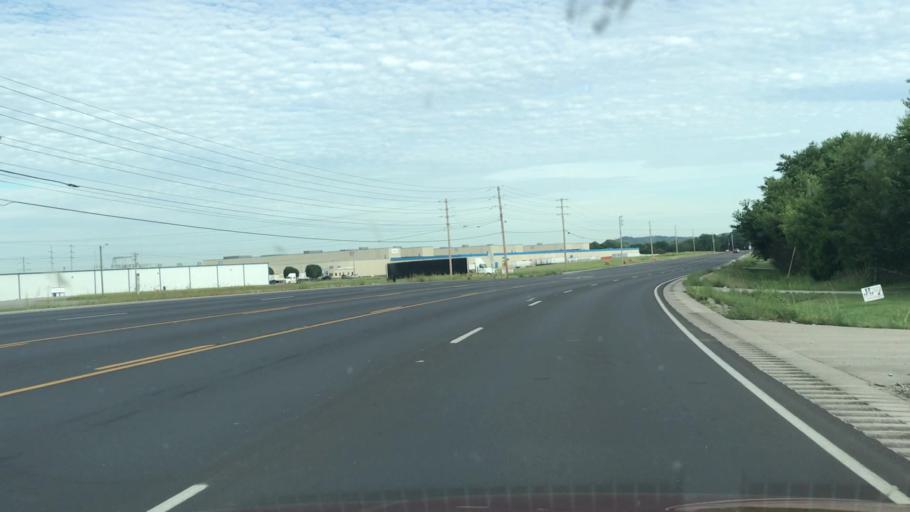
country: US
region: Kentucky
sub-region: Warren County
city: Bowling Green
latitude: 37.0337
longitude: -86.3274
